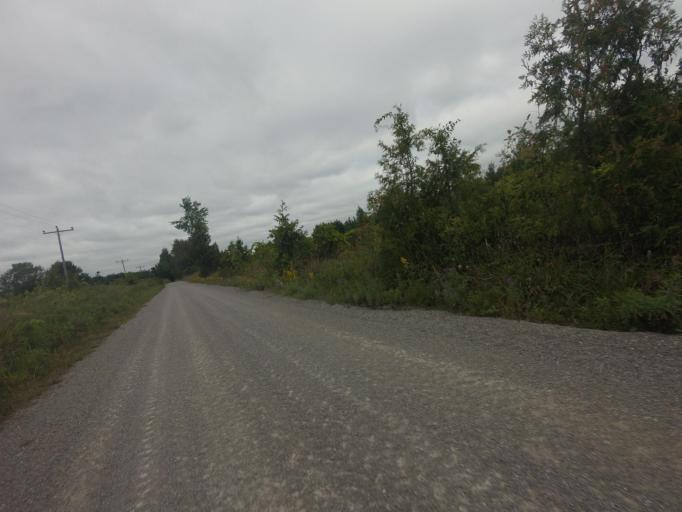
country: CA
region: Ontario
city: Omemee
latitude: 44.4635
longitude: -78.7564
